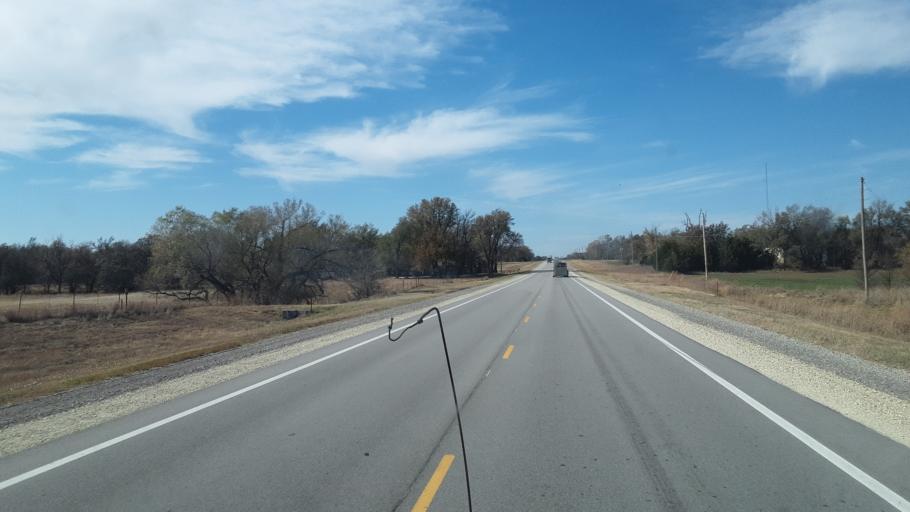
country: US
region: Kansas
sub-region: McPherson County
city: McPherson
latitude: 38.3769
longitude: -97.4939
